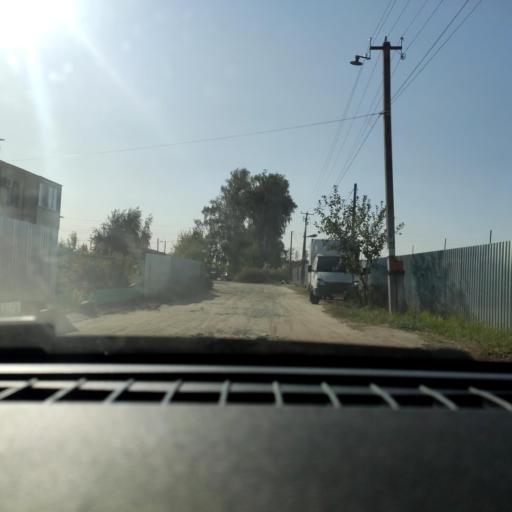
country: RU
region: Voronezj
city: Maslovka
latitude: 51.5441
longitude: 39.2194
